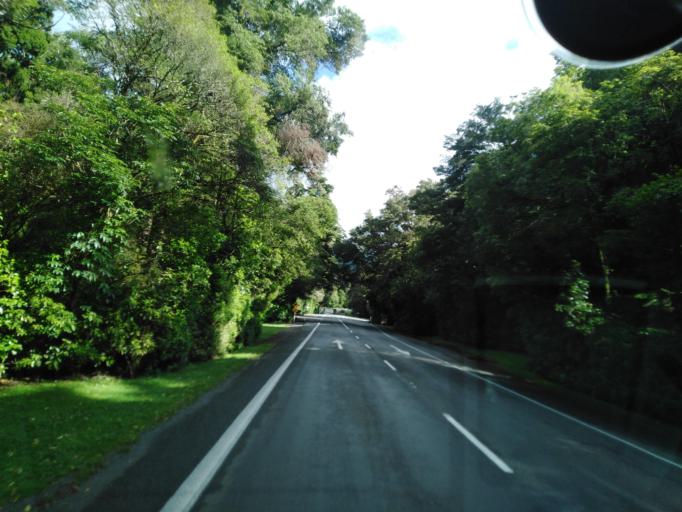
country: NZ
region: Nelson
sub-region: Nelson City
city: Nelson
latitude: -41.3002
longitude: 173.5732
